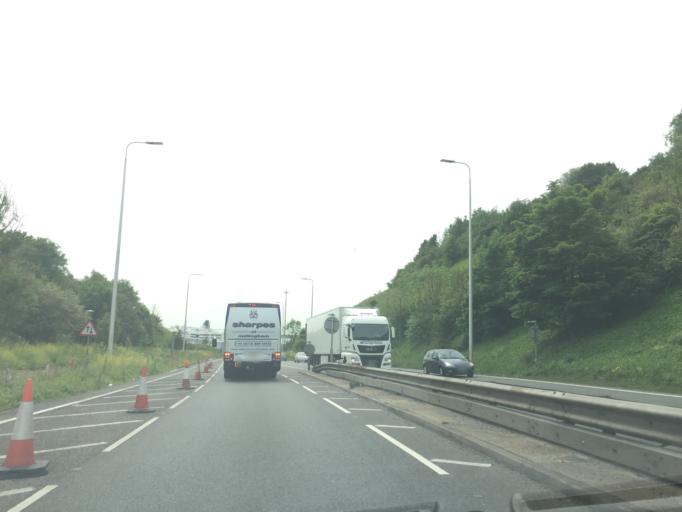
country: GB
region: England
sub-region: Kent
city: Dover
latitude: 51.1298
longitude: 1.3287
